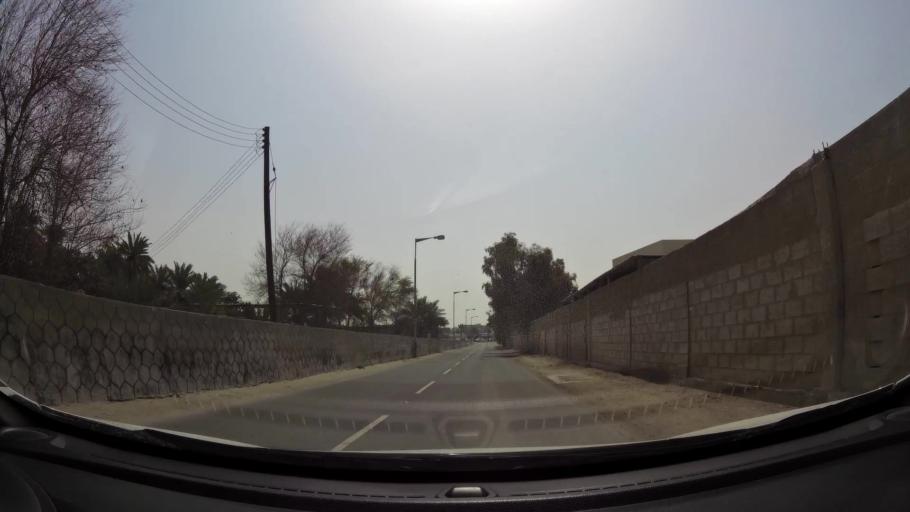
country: BH
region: Manama
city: Jidd Hafs
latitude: 26.2220
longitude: 50.5050
